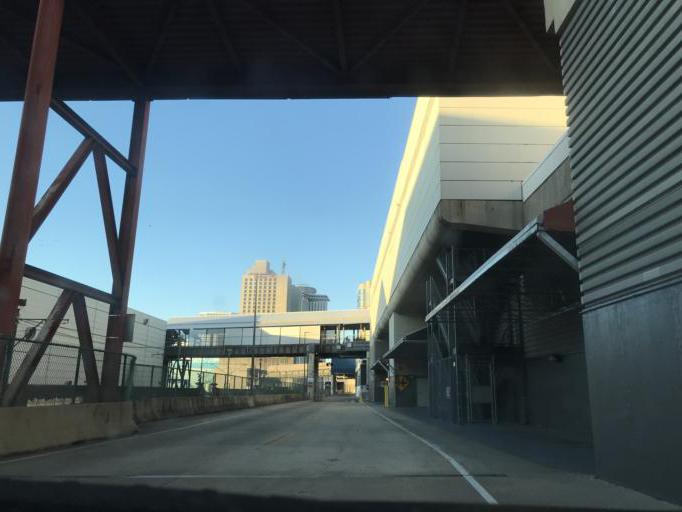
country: US
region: Louisiana
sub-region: Orleans Parish
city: New Orleans
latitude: 29.9429
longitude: -90.0622
